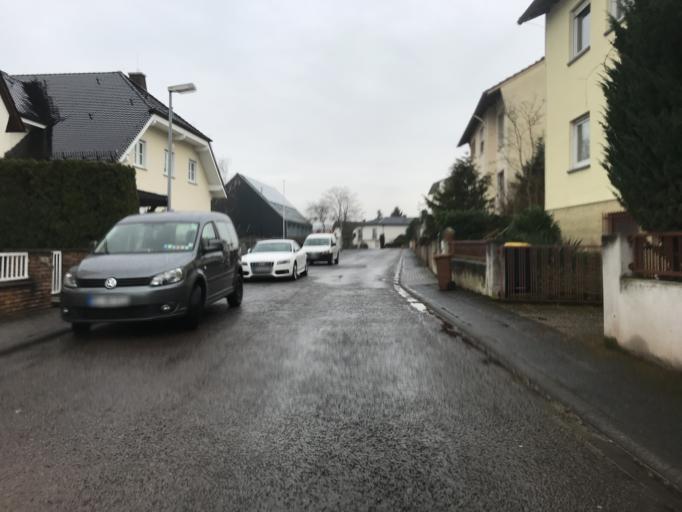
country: DE
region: Rheinland-Pfalz
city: Wackernheim
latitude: 49.9923
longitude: 8.1090
